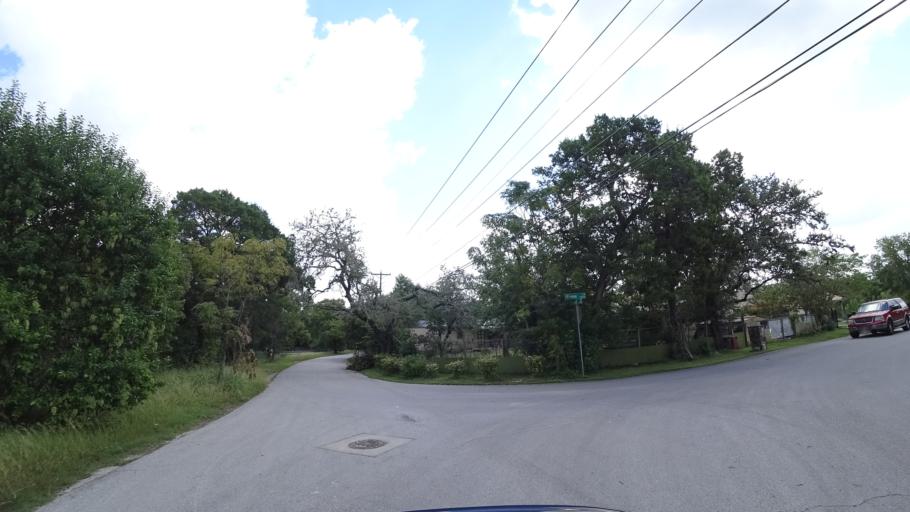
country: US
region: Texas
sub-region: Travis County
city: Onion Creek
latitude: 30.1928
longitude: -97.8031
